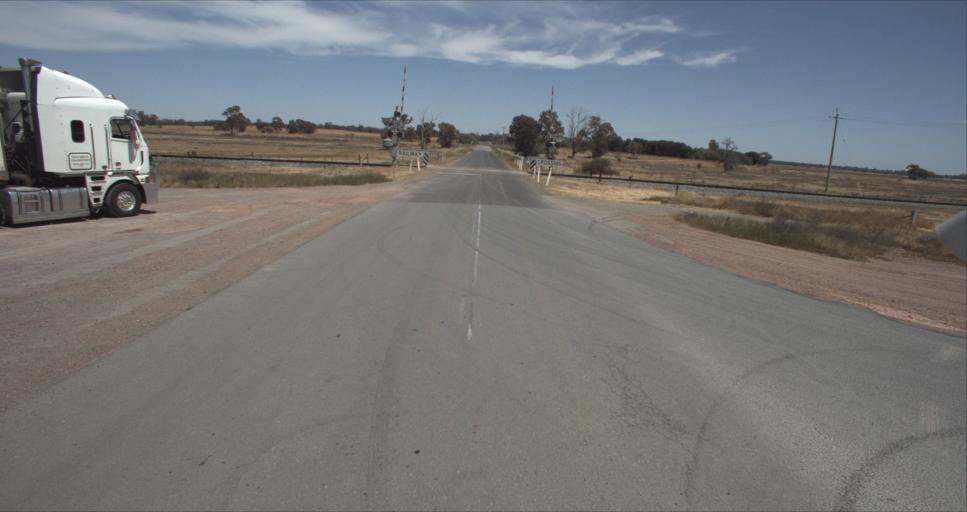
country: AU
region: New South Wales
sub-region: Leeton
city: Leeton
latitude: -34.6469
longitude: 146.4726
